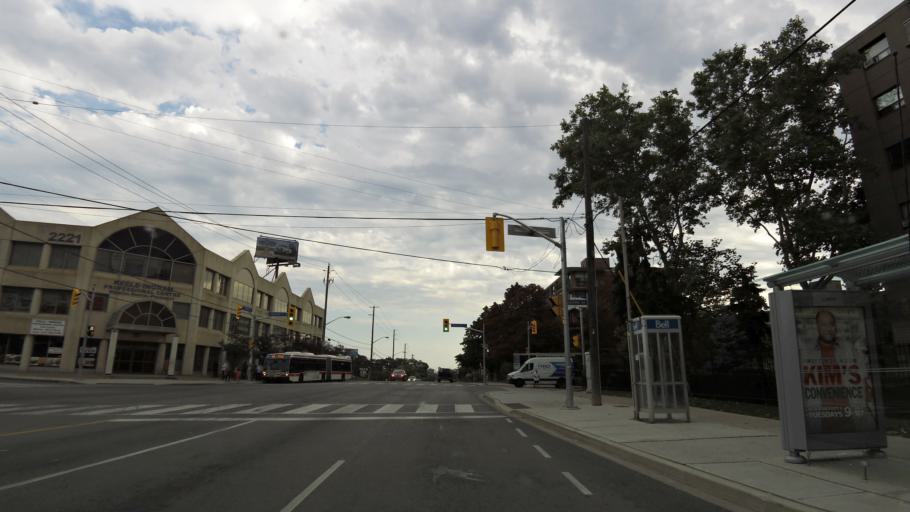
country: CA
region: Ontario
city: Toronto
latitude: 43.6996
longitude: -79.4761
